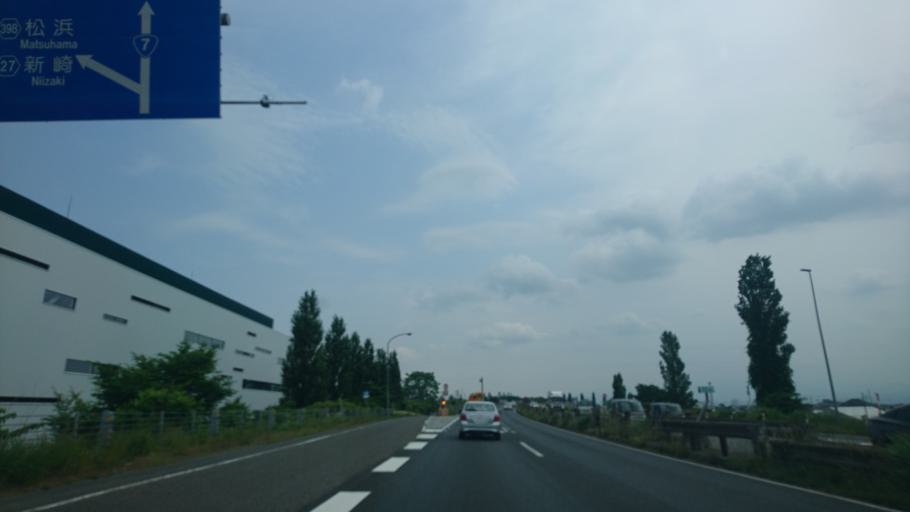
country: JP
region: Niigata
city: Kameda-honcho
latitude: 37.9359
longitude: 139.1538
